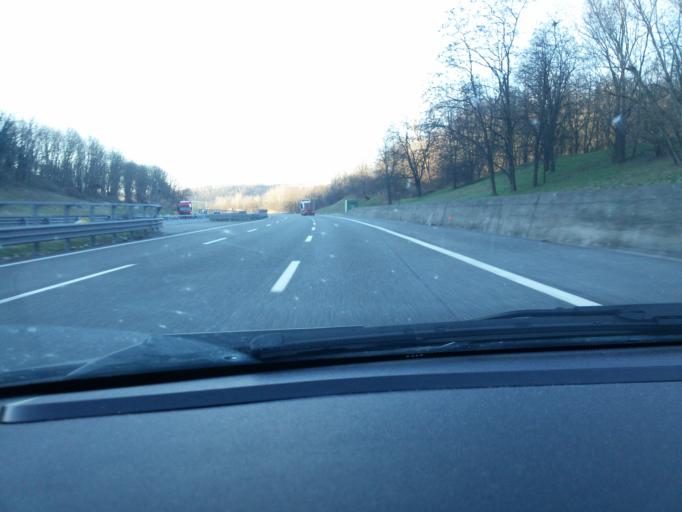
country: IT
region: Piedmont
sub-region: Provincia di Alessandria
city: San Salvatore Monferrato
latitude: 44.9986
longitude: 8.5406
